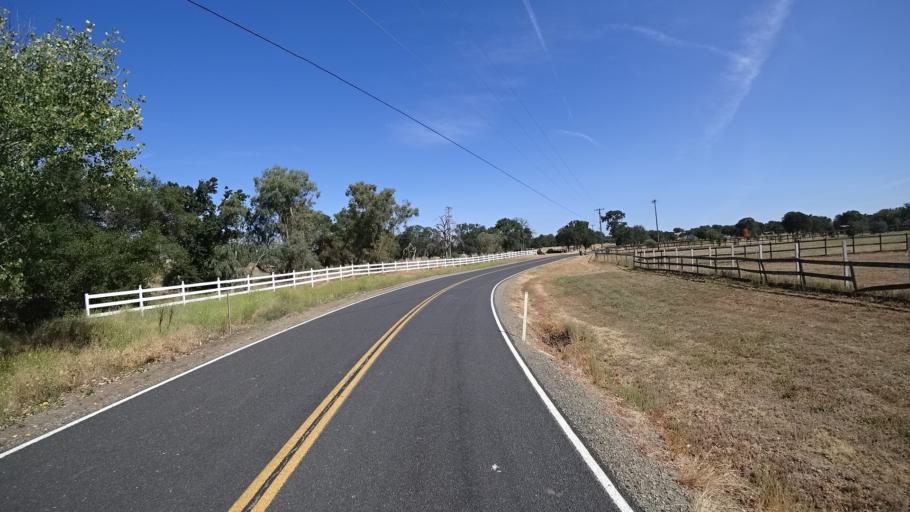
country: US
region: California
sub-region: Calaveras County
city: Rancho Calaveras
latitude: 38.1143
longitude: -120.9264
